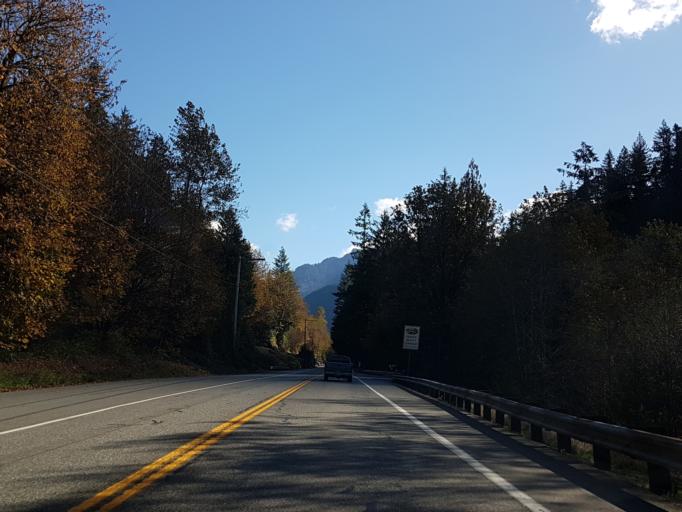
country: US
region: Washington
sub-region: Snohomish County
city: Gold Bar
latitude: 47.7982
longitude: -121.5151
